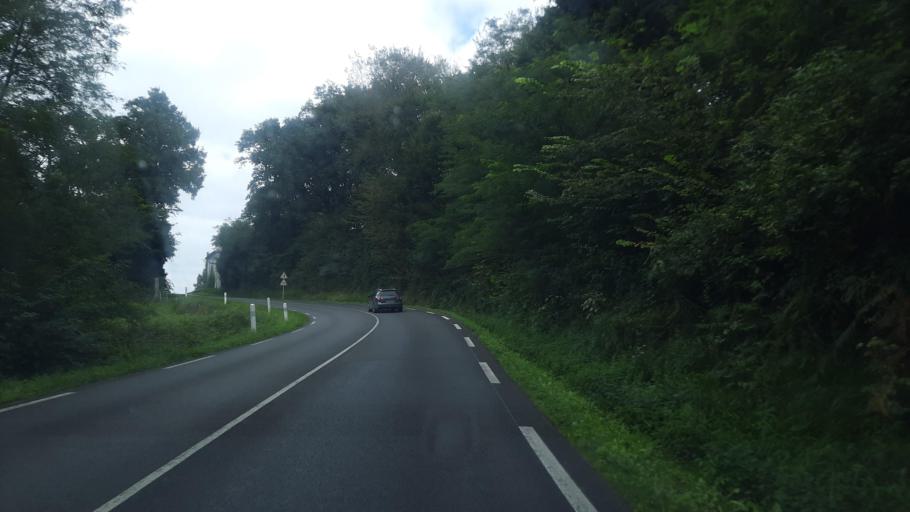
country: FR
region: Midi-Pyrenees
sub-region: Departement des Hautes-Pyrenees
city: Semeac
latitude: 43.2397
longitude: 0.1168
